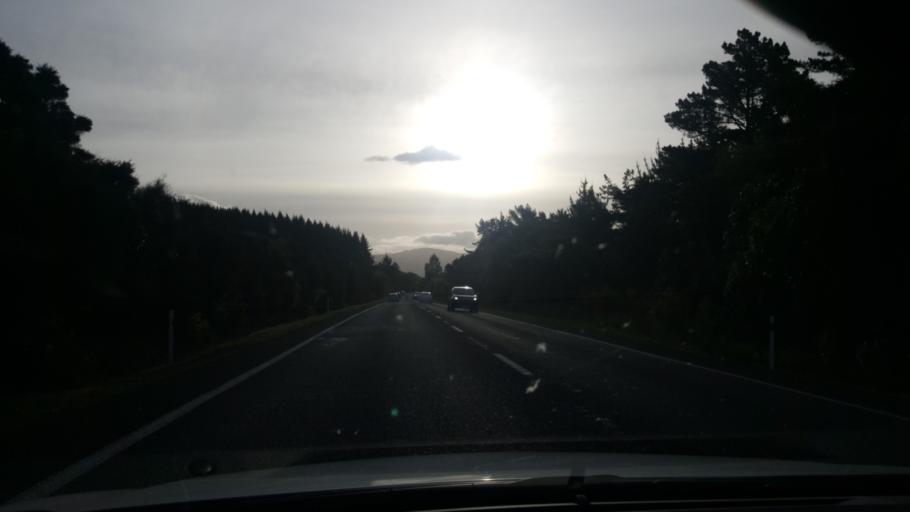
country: NZ
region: Waikato
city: Turangi
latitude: -38.9364
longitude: 175.8673
